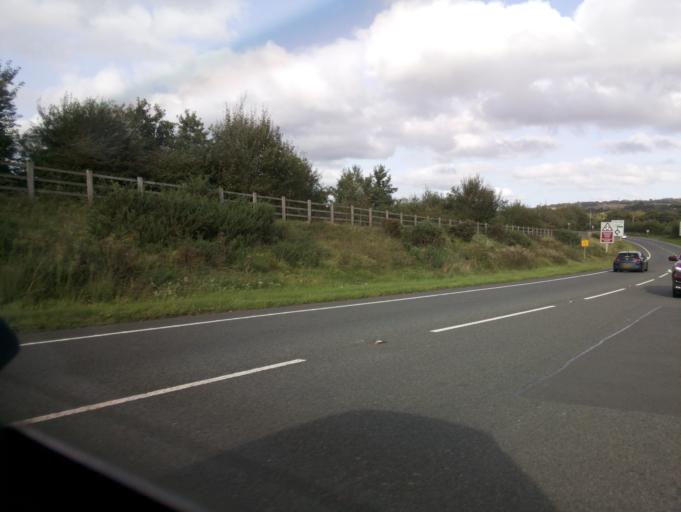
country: GB
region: Wales
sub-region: Rhondda Cynon Taf
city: Llantwit Fardre
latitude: 51.5456
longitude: -3.3400
